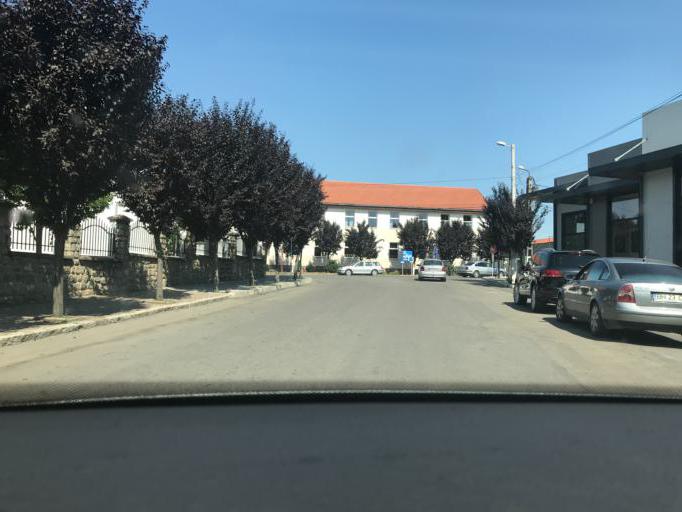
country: RO
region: Bihor
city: Margita
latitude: 47.3470
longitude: 22.3423
